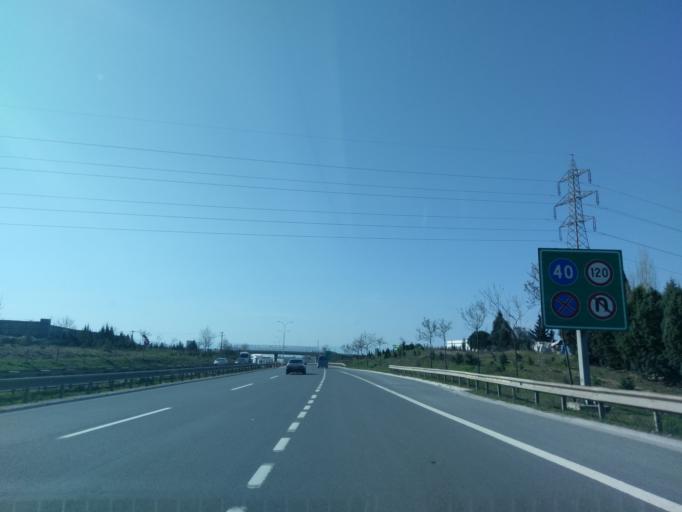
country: TR
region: Kocaeli
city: Balcik
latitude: 40.8602
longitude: 29.3793
